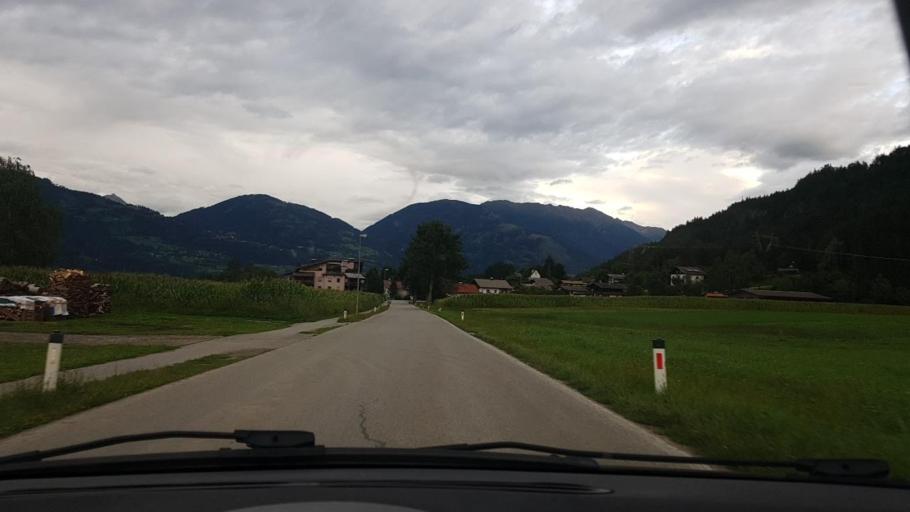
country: AT
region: Tyrol
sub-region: Politischer Bezirk Lienz
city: Amlach
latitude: 46.8140
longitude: 12.7668
